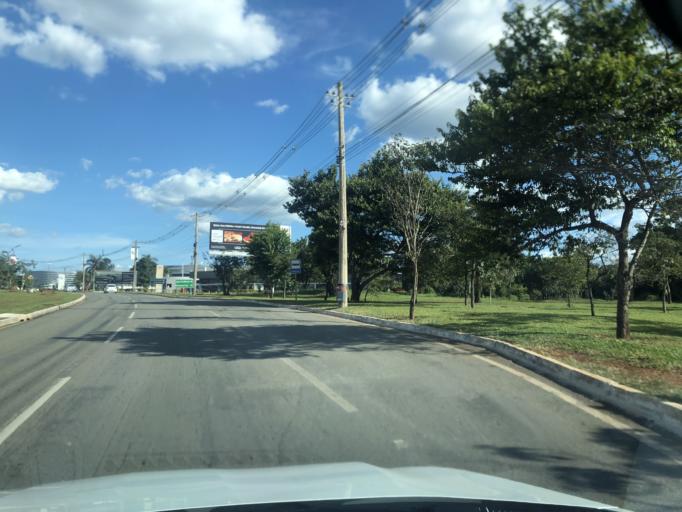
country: BR
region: Federal District
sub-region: Brasilia
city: Brasilia
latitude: -15.8688
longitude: -47.9367
